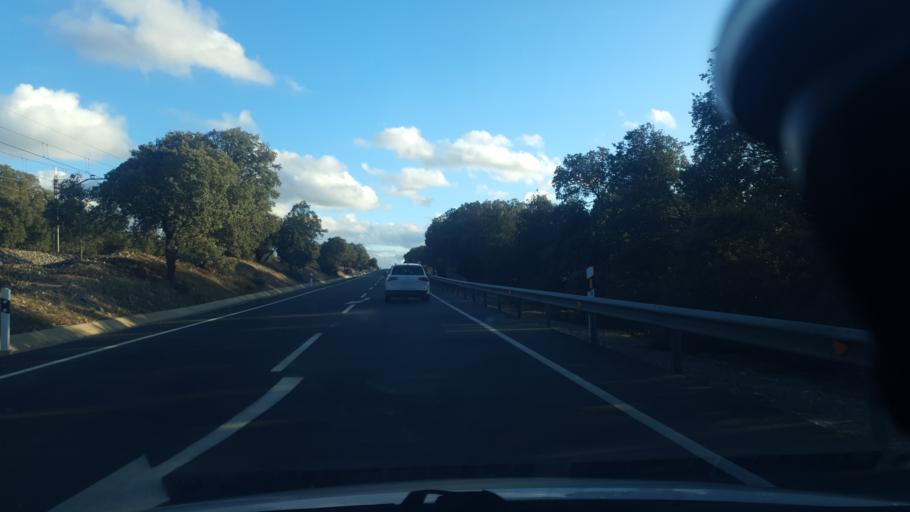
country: ES
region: Castille and Leon
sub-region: Provincia de Avila
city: Mingorria
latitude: 40.7135
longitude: -4.6734
